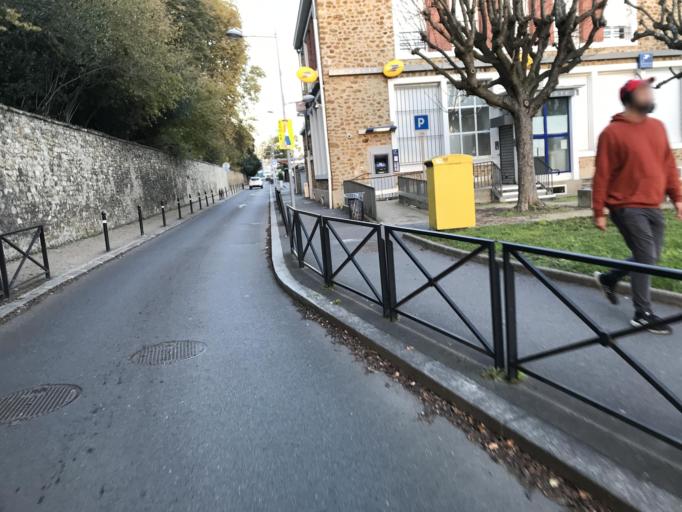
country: FR
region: Ile-de-France
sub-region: Departement de l'Essonne
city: Athis-Mons
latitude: 48.7061
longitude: 2.3852
